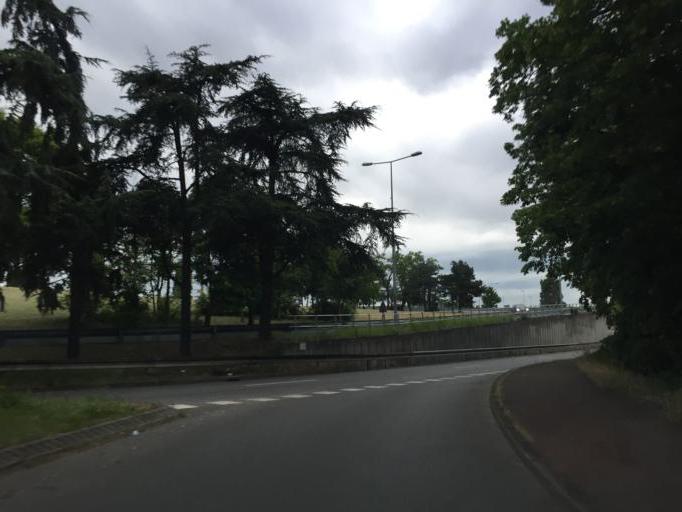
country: FR
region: Rhone-Alpes
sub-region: Departement du Rhone
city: Bron
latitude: 45.7355
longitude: 4.9037
